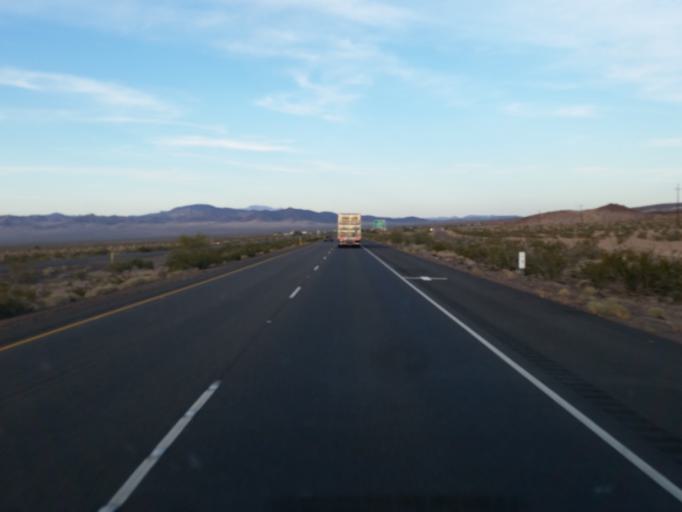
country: US
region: California
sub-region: San Bernardino County
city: Joshua Tree
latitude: 34.7241
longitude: -116.1894
